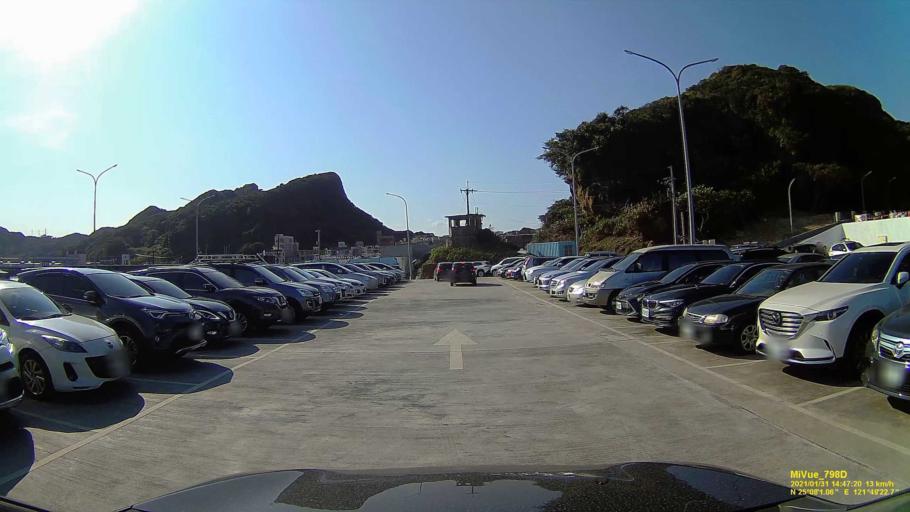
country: TW
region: Taiwan
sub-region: Keelung
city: Keelung
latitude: 25.1335
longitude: 121.8229
